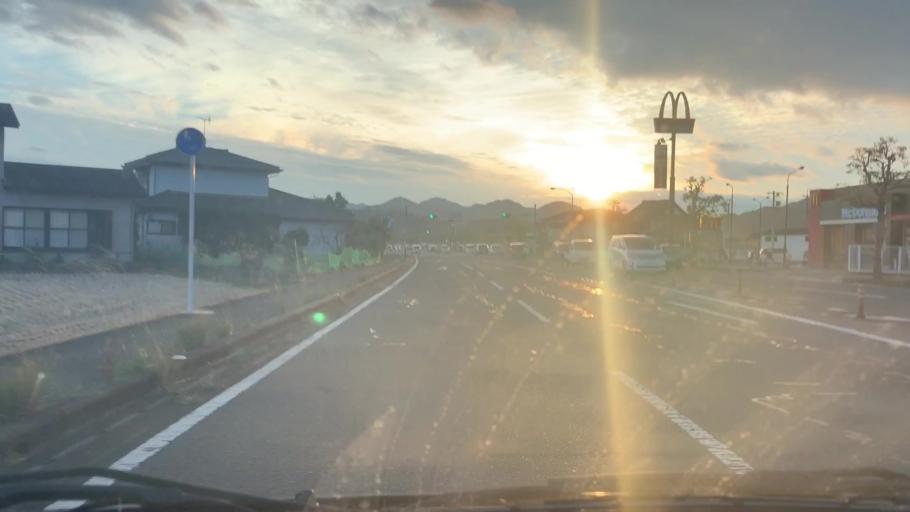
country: JP
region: Saga Prefecture
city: Kashima
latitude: 33.1209
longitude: 130.0932
